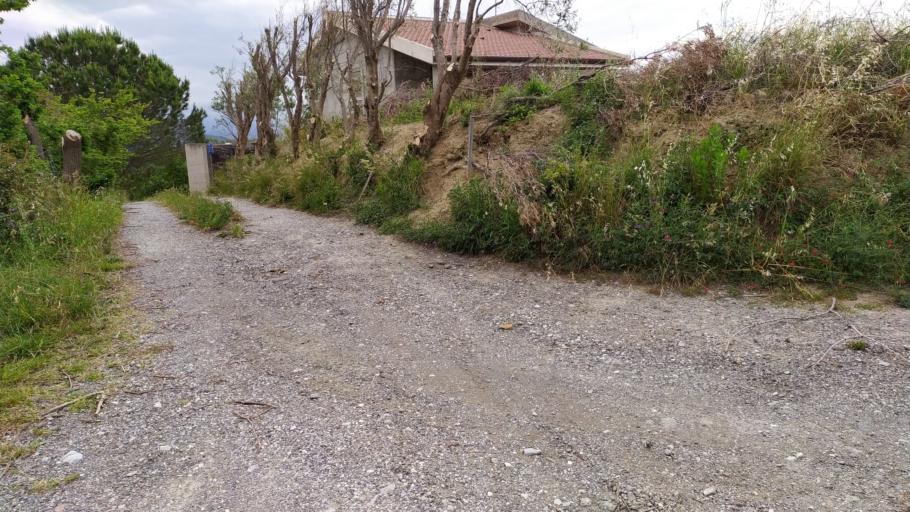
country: IT
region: Sicily
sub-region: Messina
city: Santa Lucia del Mela
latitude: 38.1601
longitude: 15.2953
